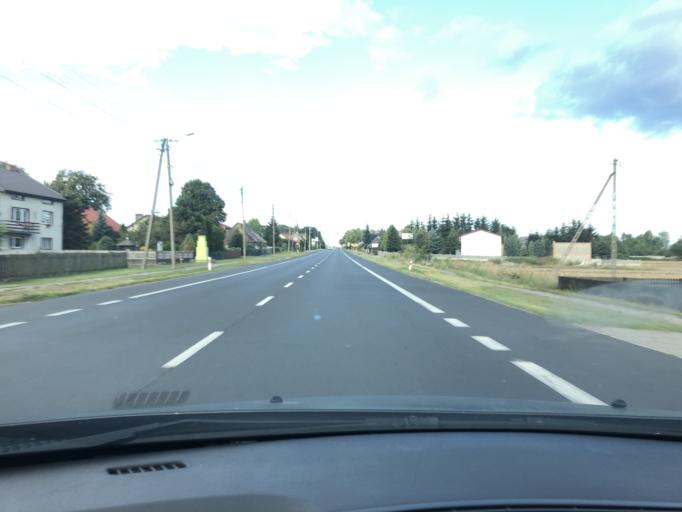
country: PL
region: Lodz Voivodeship
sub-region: Powiat wieruszowski
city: Sokolniki
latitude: 51.3046
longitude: 18.3060
